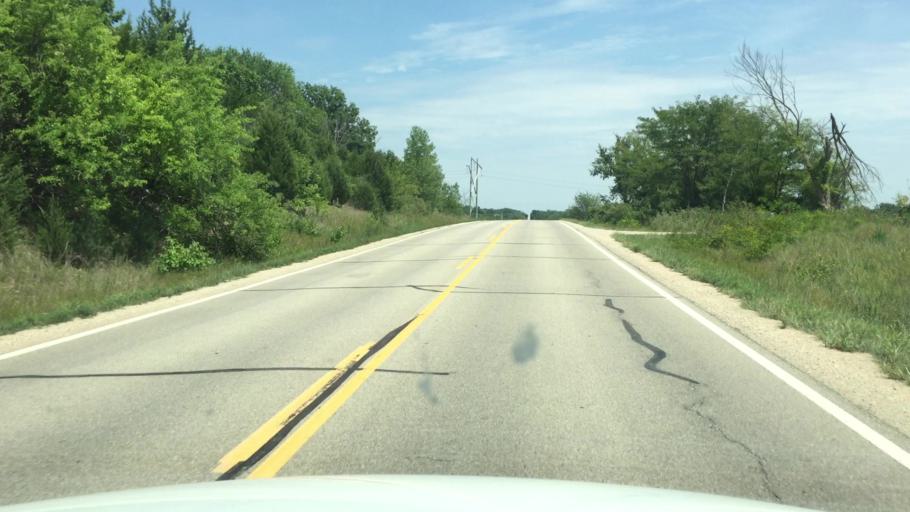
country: US
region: Kansas
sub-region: Osage County
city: Overbrook
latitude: 38.9712
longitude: -95.4736
